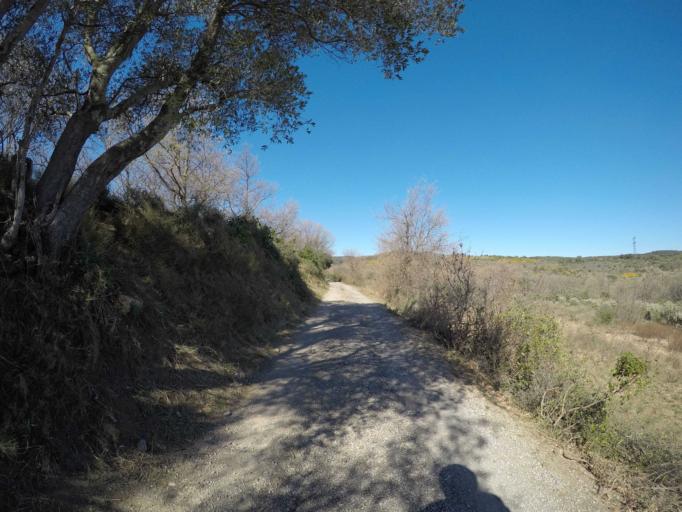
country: FR
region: Languedoc-Roussillon
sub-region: Departement des Pyrenees-Orientales
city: Millas
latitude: 42.7079
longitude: 2.6679
